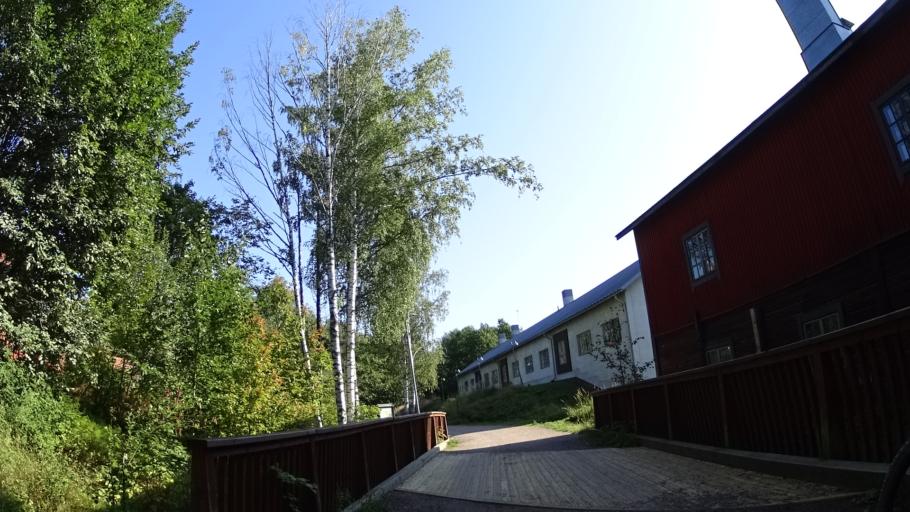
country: FI
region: Uusimaa
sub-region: Helsinki
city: Vantaa
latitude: 60.2445
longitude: 25.0090
